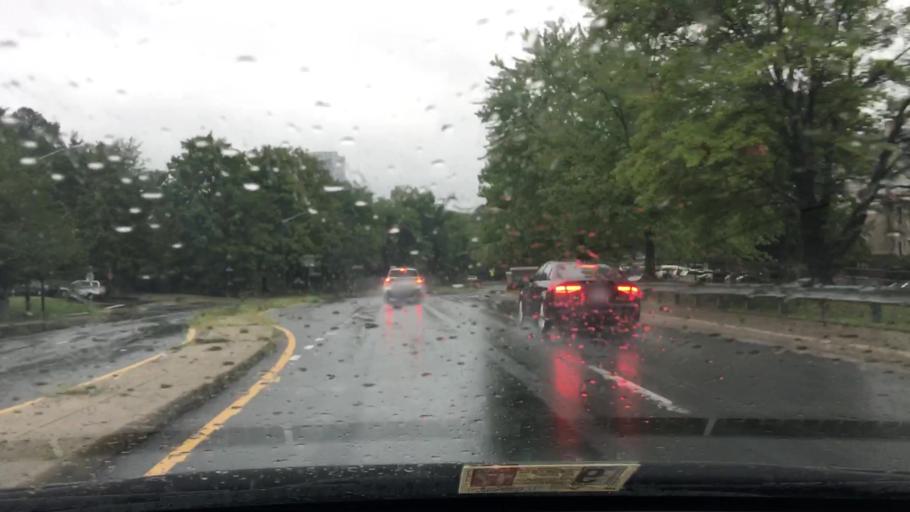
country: US
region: Virginia
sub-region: Fairfax County
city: Tysons Corner
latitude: 38.9200
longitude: -77.2388
